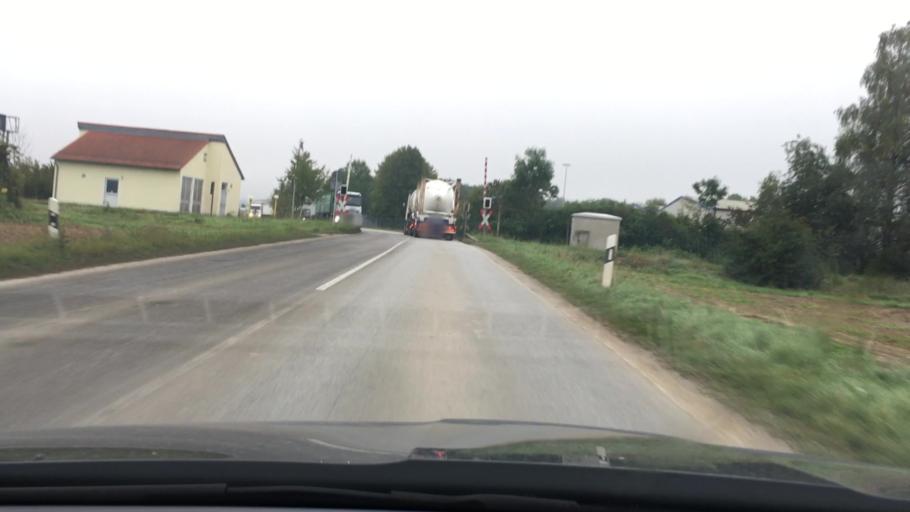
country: DE
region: Bavaria
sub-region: Lower Bavaria
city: Plattling
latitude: 48.7923
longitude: 12.8862
